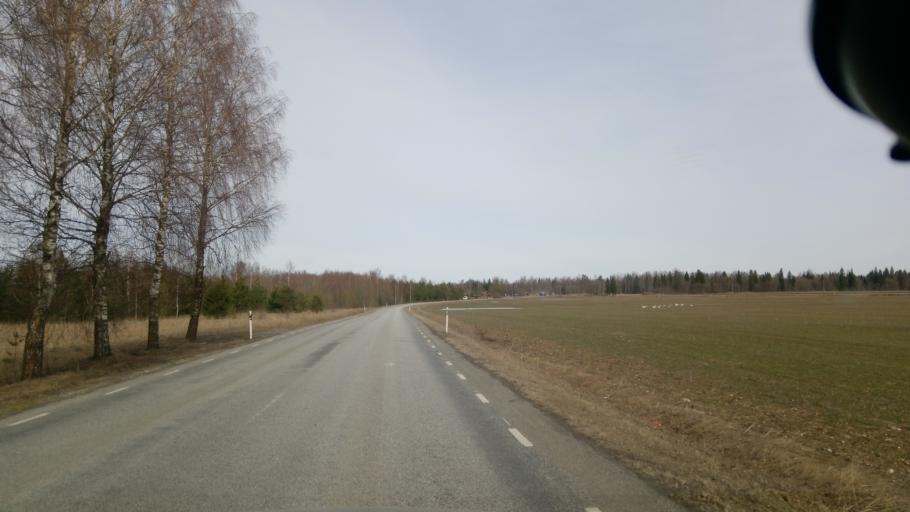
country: EE
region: Raplamaa
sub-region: Rapla vald
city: Rapla
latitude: 59.0348
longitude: 24.8355
